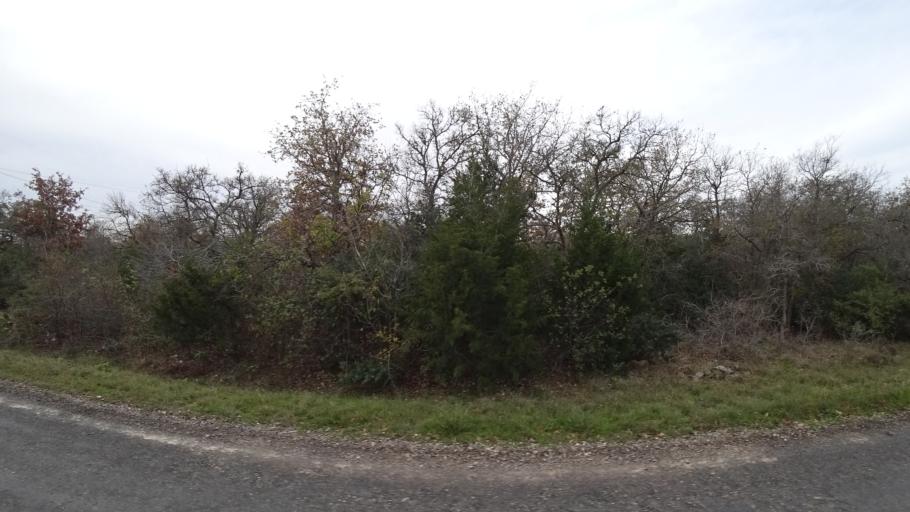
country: US
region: Texas
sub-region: Travis County
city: Garfield
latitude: 30.1051
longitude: -97.5679
